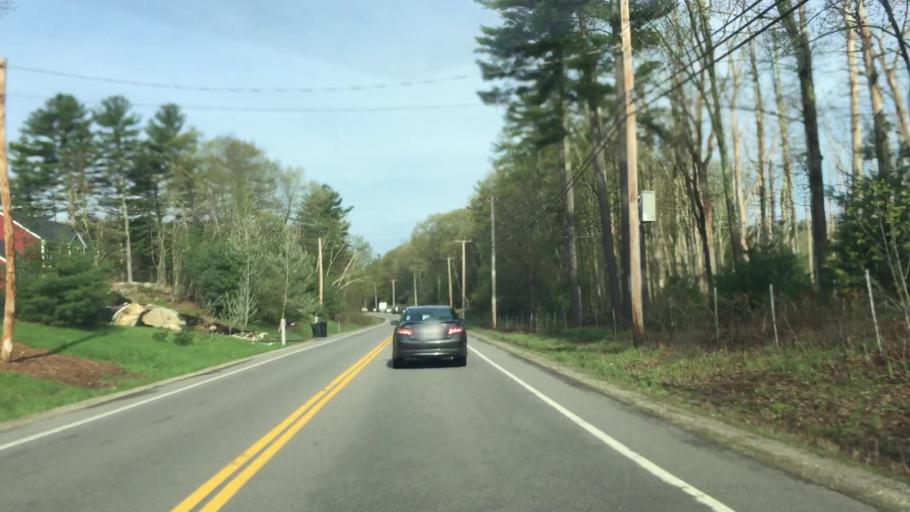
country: US
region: New Hampshire
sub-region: Hillsborough County
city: Pelham
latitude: 42.7036
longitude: -71.3578
